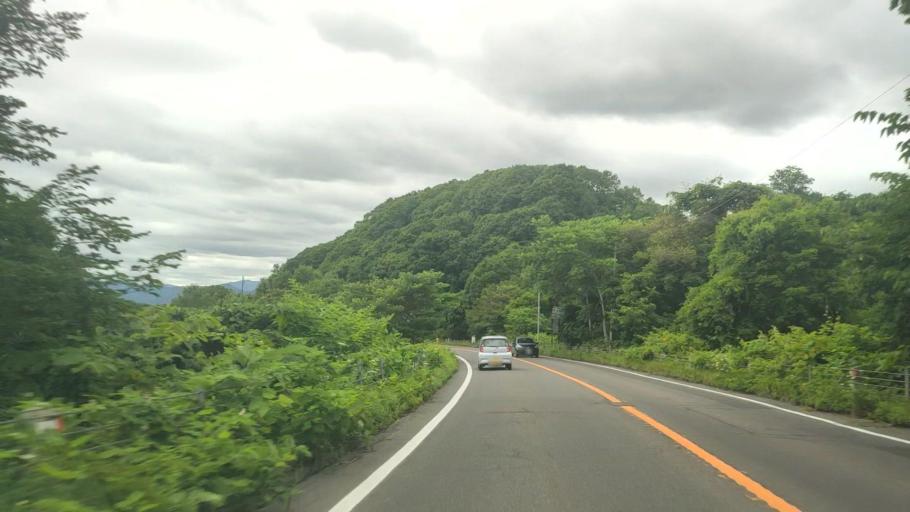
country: JP
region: Hokkaido
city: Date
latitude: 42.5740
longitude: 140.7305
